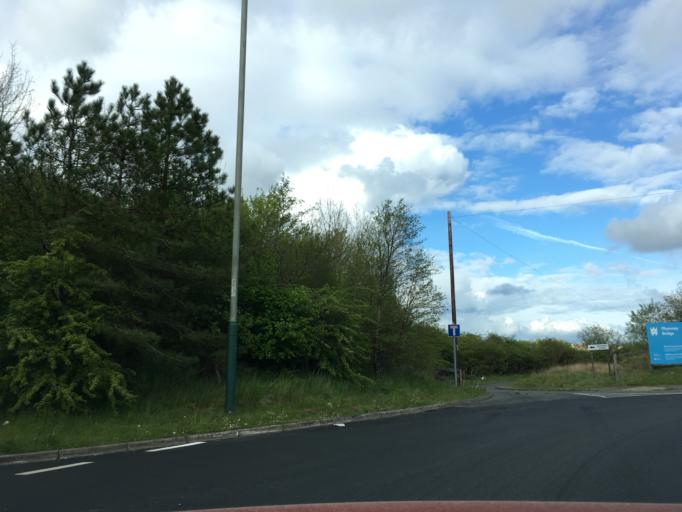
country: GB
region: Wales
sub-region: Caerphilly County Borough
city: Rhymney
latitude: 51.7776
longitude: -3.3023
